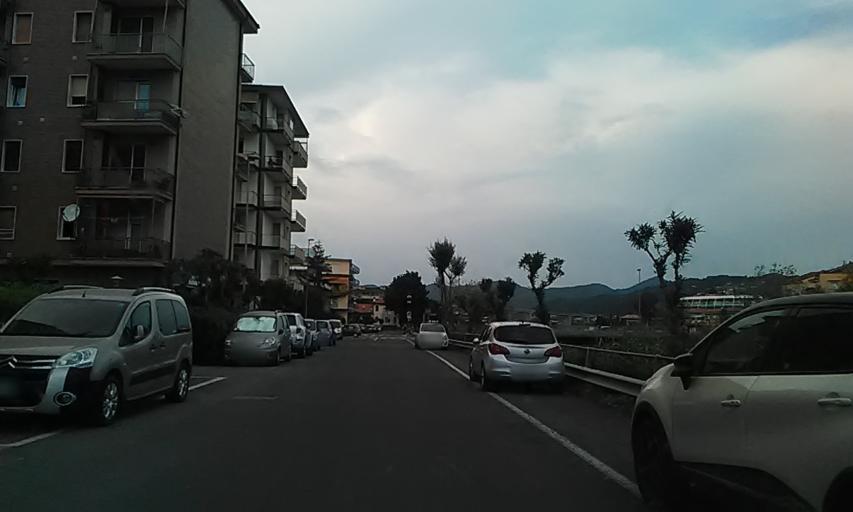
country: IT
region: Liguria
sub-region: Provincia di Savona
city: Andora
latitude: 43.9520
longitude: 8.1424
